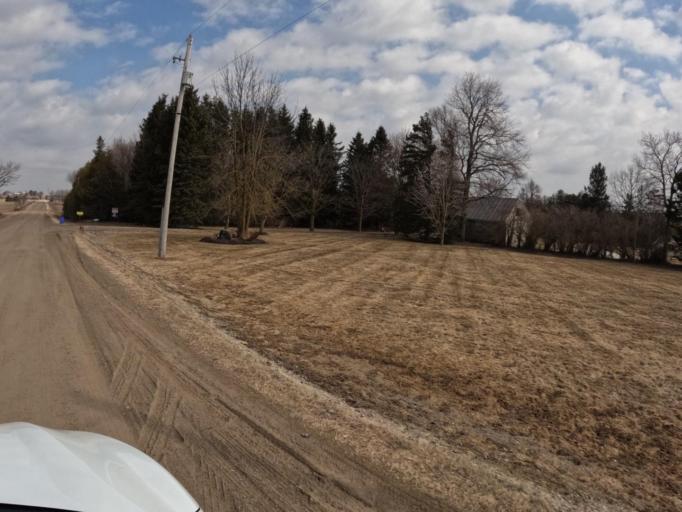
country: CA
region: Ontario
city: Orangeville
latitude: 43.9199
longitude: -80.2393
